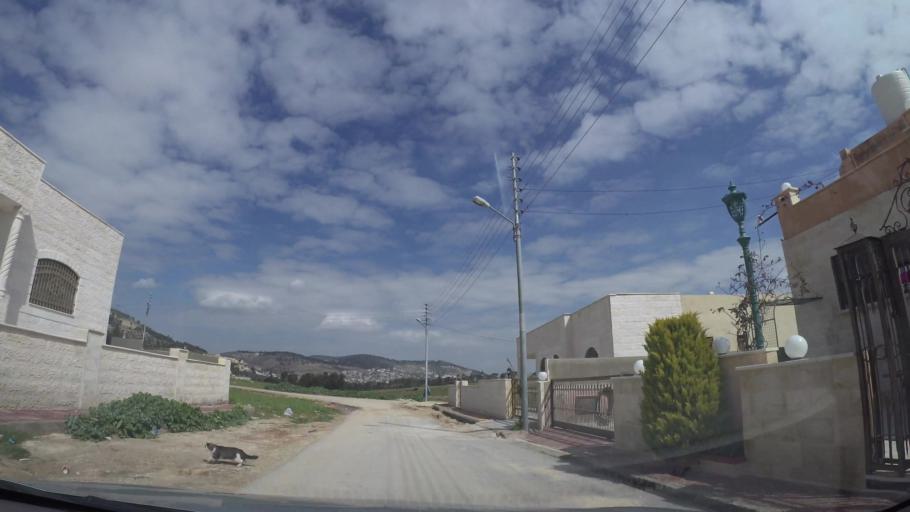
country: JO
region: Amman
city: Al Jubayhah
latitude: 32.0664
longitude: 35.8209
